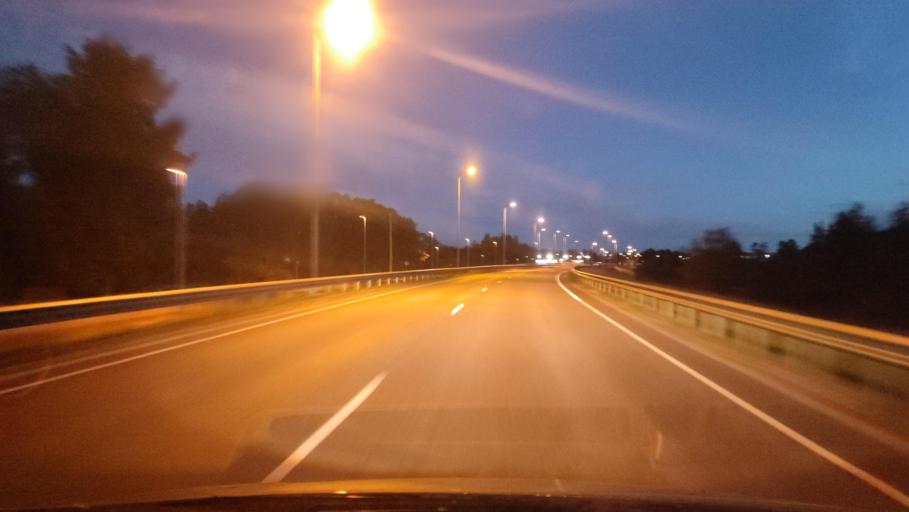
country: EE
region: Paernumaa
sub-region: Paernu linn
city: Parnu
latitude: 58.3988
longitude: 24.4659
